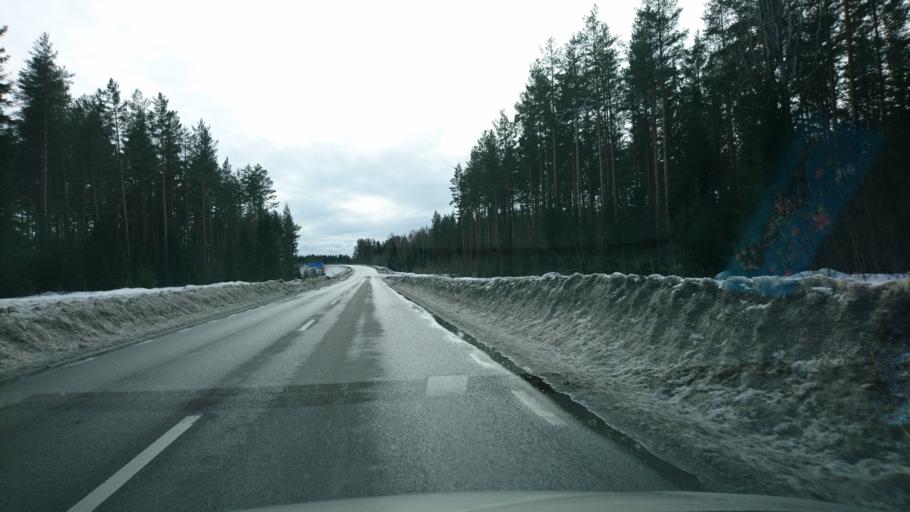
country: SE
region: Vaesternorrland
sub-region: Timra Kommun
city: Bergeforsen
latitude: 62.5550
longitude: 17.4063
